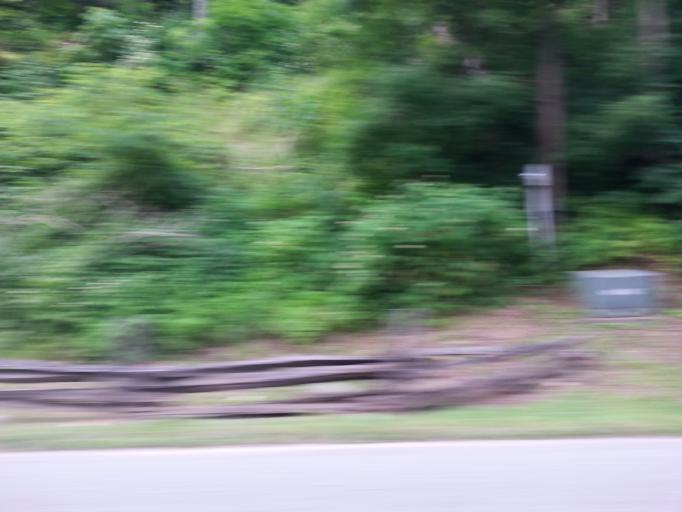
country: US
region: Tennessee
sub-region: Sevier County
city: Pigeon Forge
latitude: 35.6611
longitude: -83.7096
